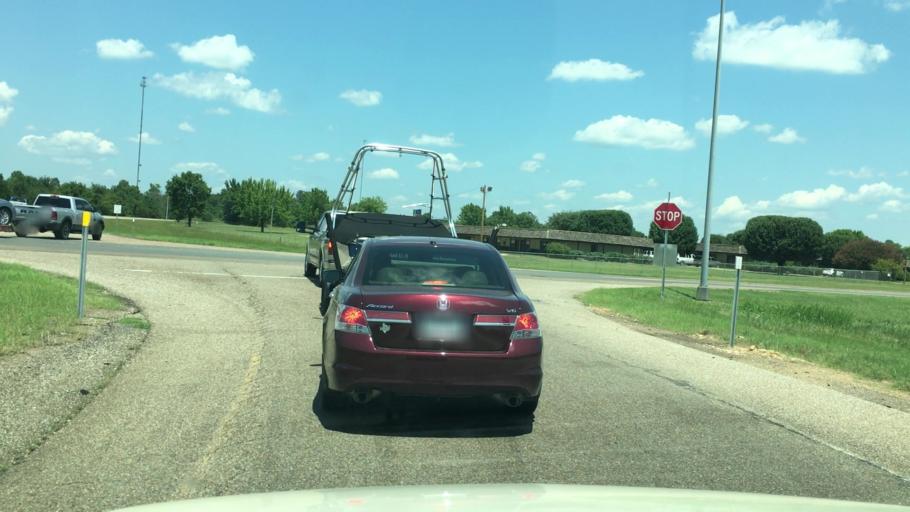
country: US
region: Arkansas
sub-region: Nevada County
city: Prescott
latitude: 33.8101
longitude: -93.4204
